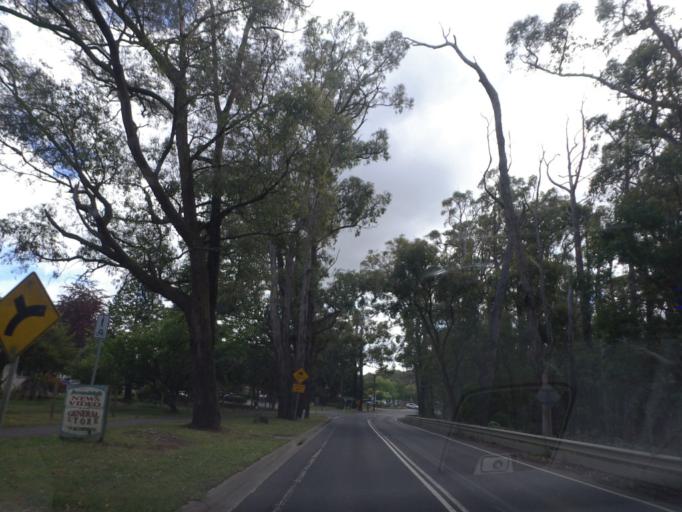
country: AU
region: Victoria
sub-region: Cardinia
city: Emerald
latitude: -37.9221
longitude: 145.4654
